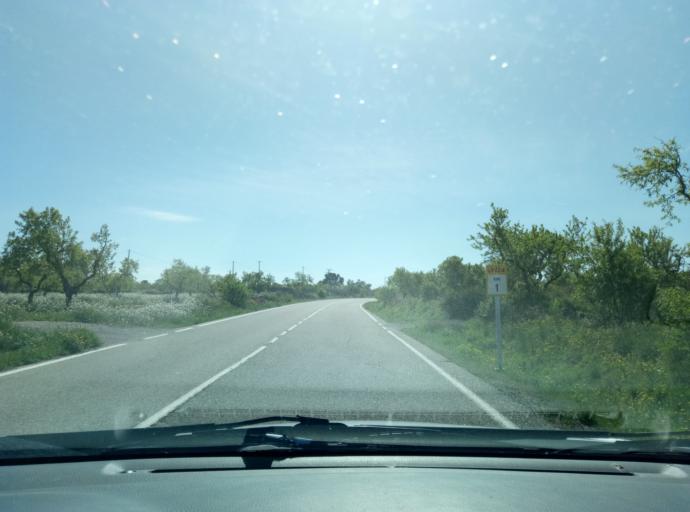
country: ES
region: Catalonia
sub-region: Provincia de Lleida
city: Vallbona de les Monges
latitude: 41.5457
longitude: 1.0273
